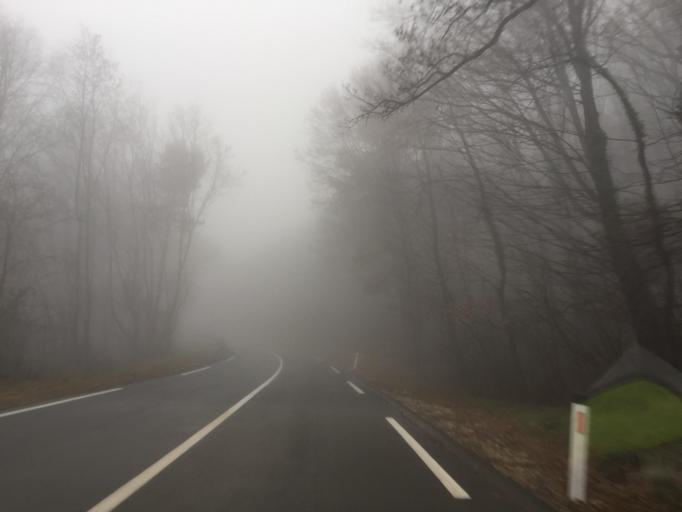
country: SI
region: Ajdovscina
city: Lokavec
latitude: 45.9311
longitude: 13.8877
